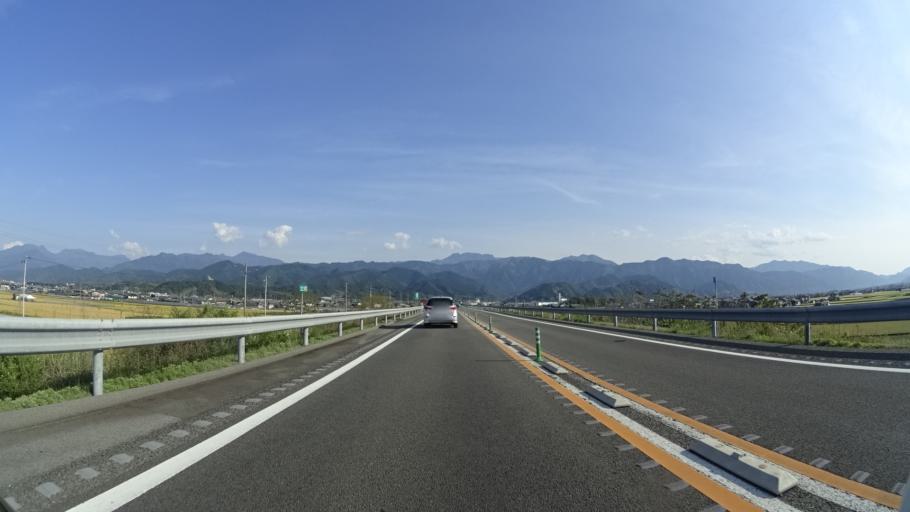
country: JP
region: Ehime
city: Saijo
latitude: 33.9050
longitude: 133.0750
